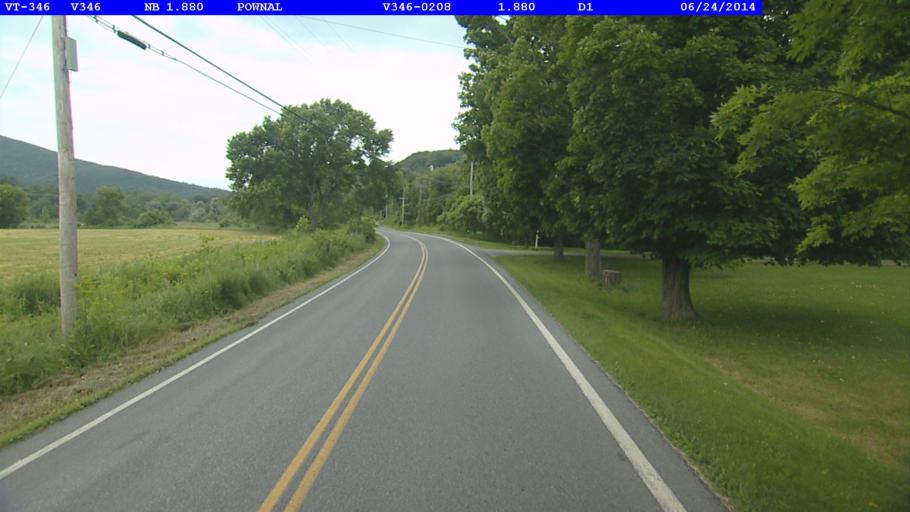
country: US
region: Massachusetts
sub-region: Berkshire County
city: Williamstown
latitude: 42.7866
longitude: -73.2494
